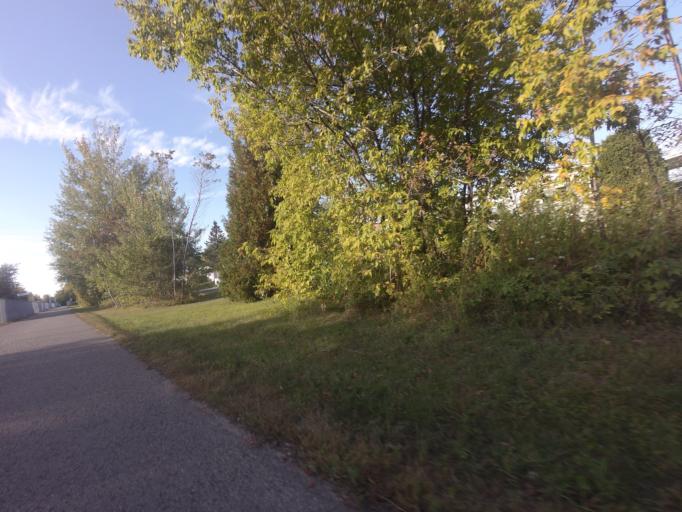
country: CA
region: Quebec
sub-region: Laurentides
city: Saint-Jerome
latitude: 45.7611
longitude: -73.9845
